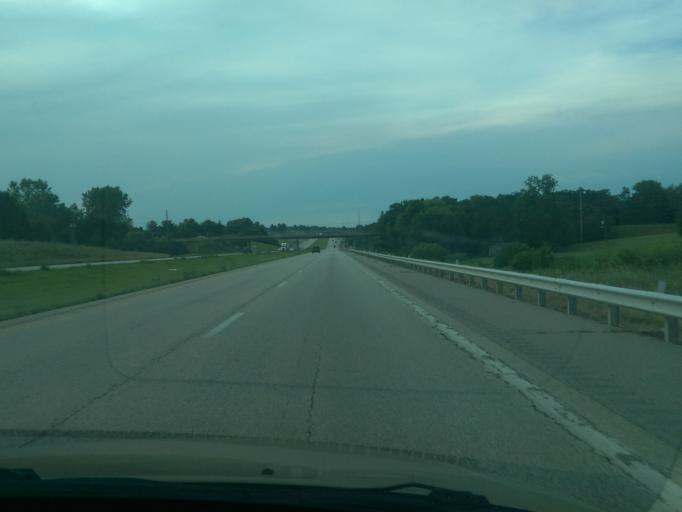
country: US
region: Missouri
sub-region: Andrew County
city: Country Club Village
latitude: 39.8044
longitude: -94.8000
